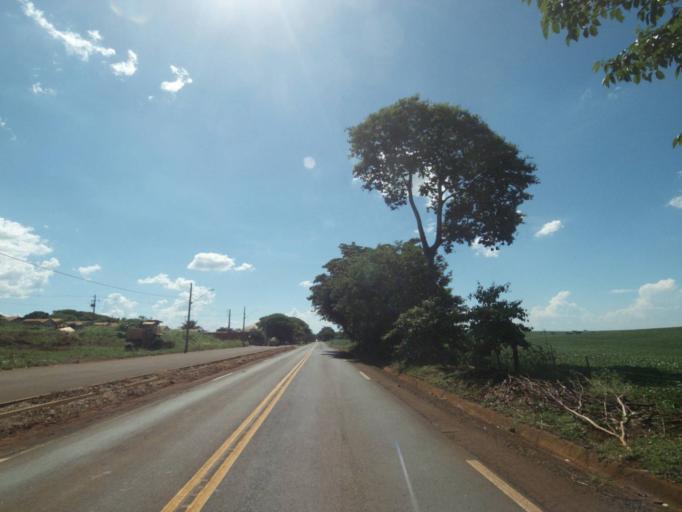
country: BR
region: Parana
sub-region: Sertanopolis
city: Sertanopolis
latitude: -23.0345
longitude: -50.8101
